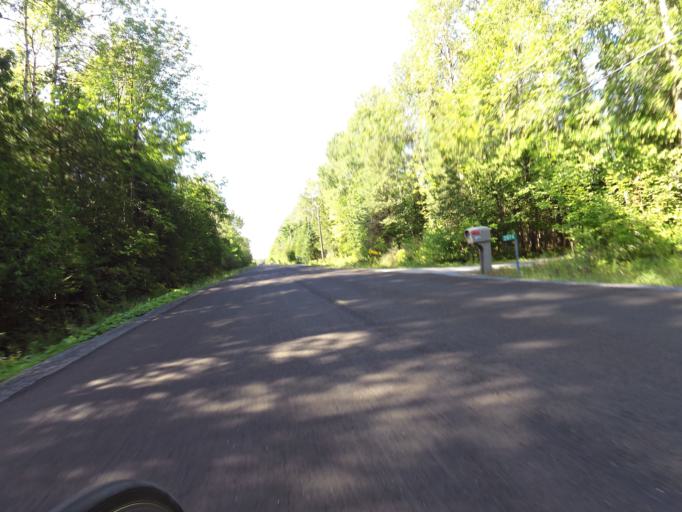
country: CA
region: Ontario
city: Bells Corners
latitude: 45.4623
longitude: -75.9778
